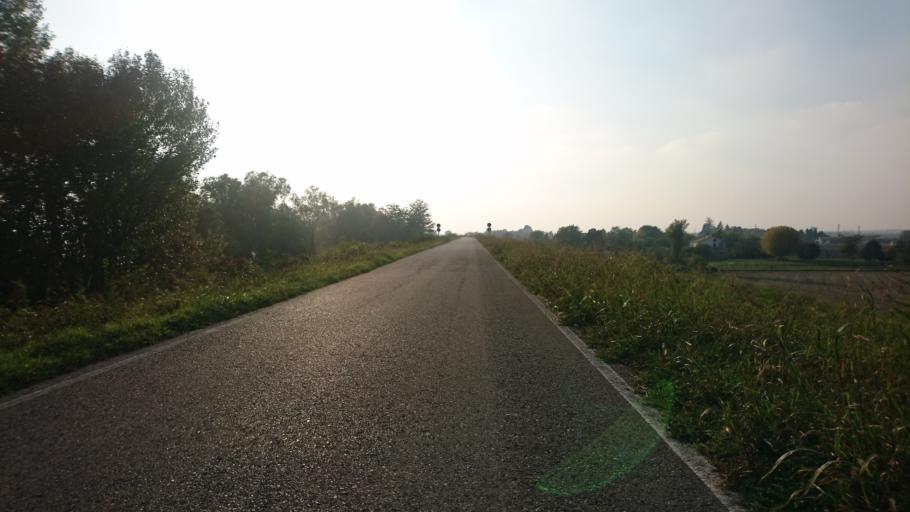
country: IT
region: Veneto
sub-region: Provincia di Rovigo
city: Canaro
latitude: 44.9182
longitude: 11.6771
